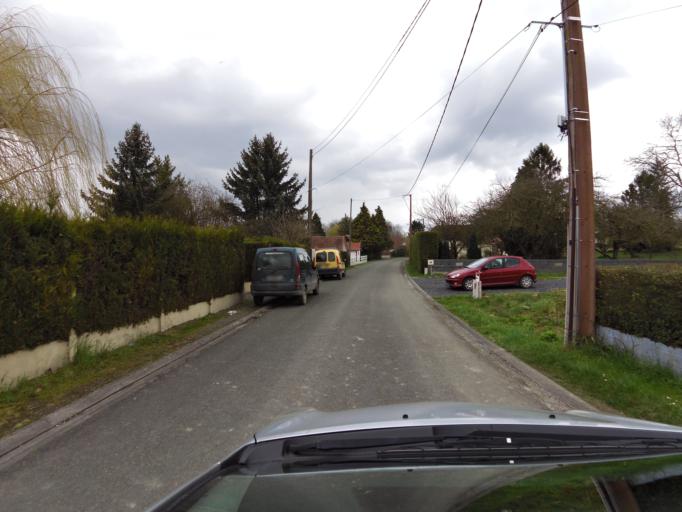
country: FR
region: Picardie
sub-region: Departement de la Somme
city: Bray-sur-Somme
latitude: 49.9371
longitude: 2.8162
